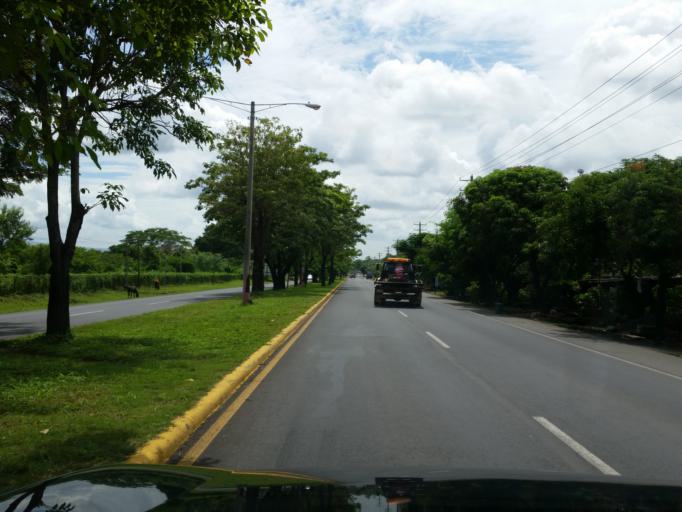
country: NI
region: Managua
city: Tipitapa
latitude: 12.1526
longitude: -86.1502
